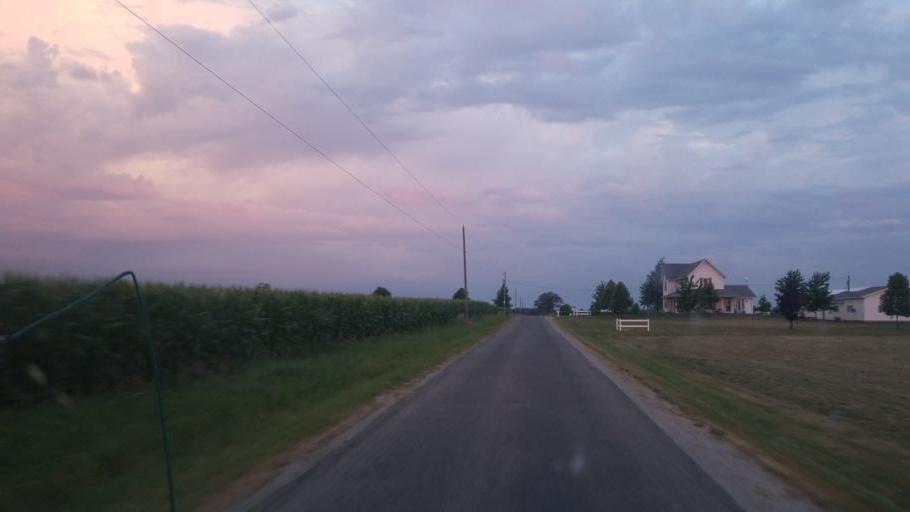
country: US
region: Ohio
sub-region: Defiance County
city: Hicksville
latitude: 41.3536
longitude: -84.7934
